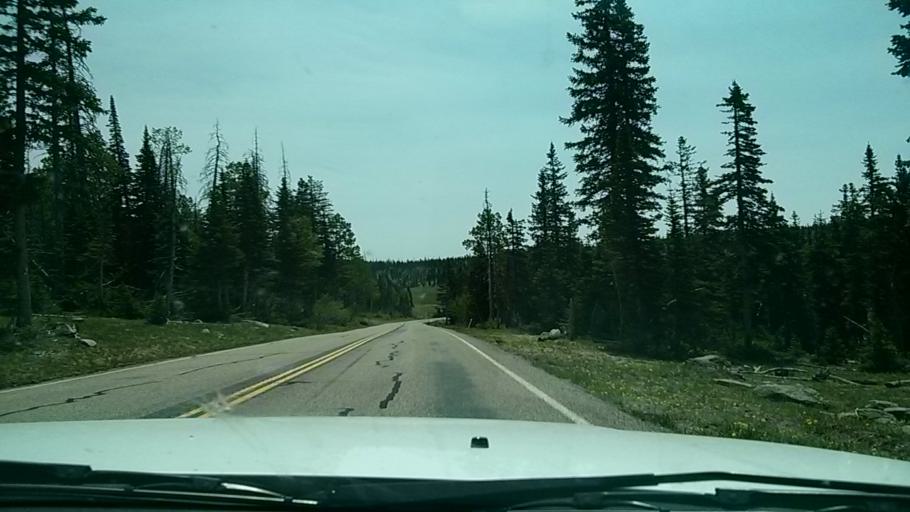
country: US
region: Utah
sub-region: Iron County
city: Cedar City
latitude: 37.5766
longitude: -112.8411
